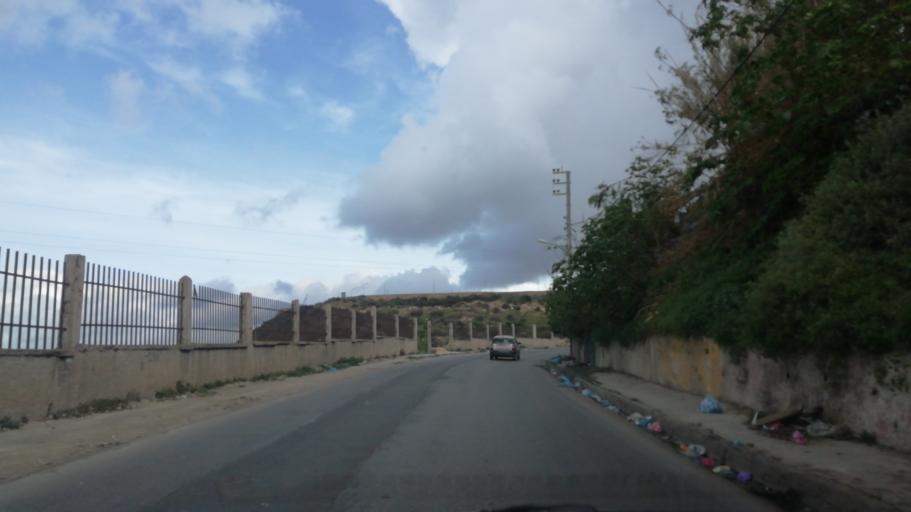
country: DZ
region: Oran
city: Oran
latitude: 35.6931
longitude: -0.6595
